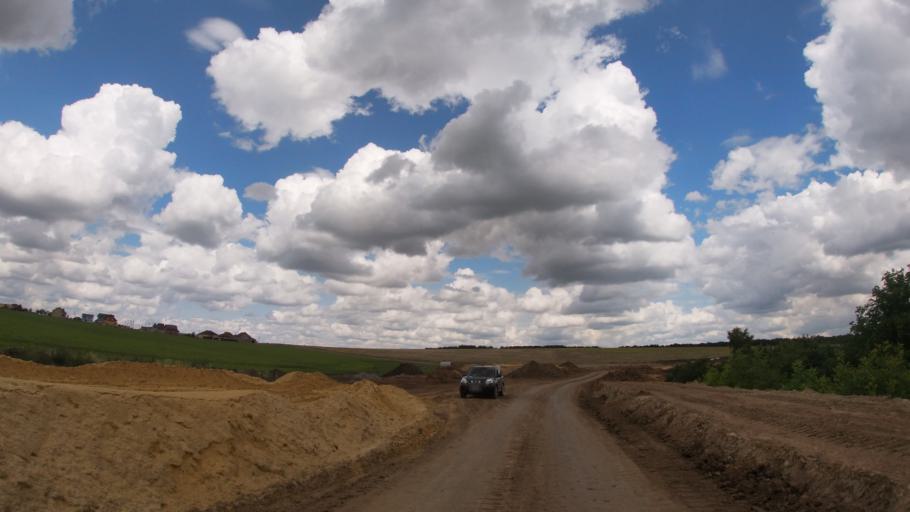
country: RU
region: Belgorod
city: Mayskiy
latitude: 50.5170
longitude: 36.4917
